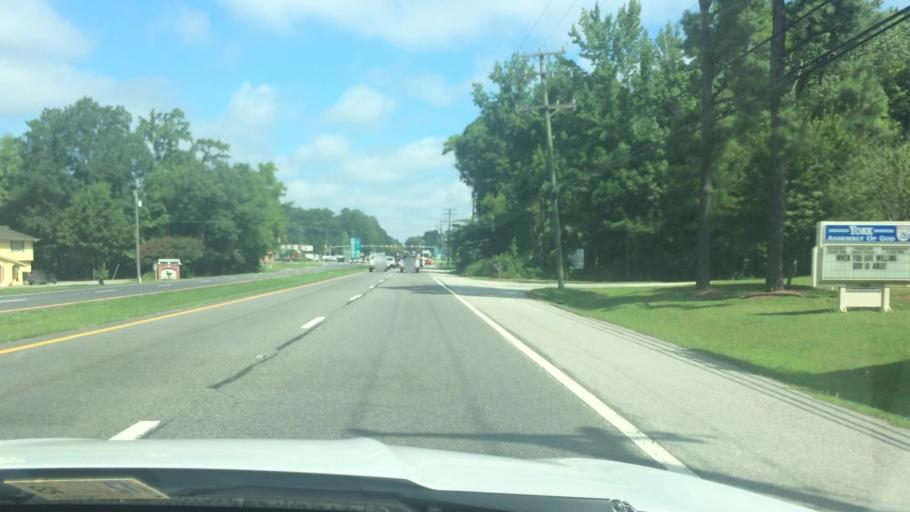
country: US
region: Virginia
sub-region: York County
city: Yorktown
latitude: 37.1871
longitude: -76.4858
